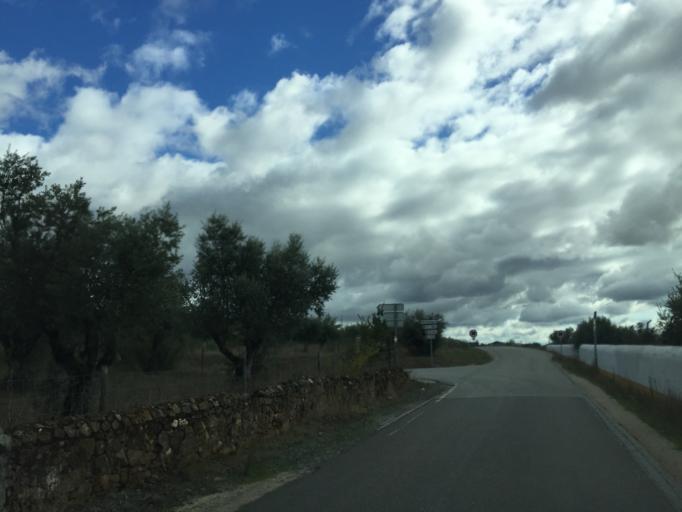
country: PT
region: Portalegre
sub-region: Alter do Chao
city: Alter do Chao
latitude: 39.2213
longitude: -7.6721
